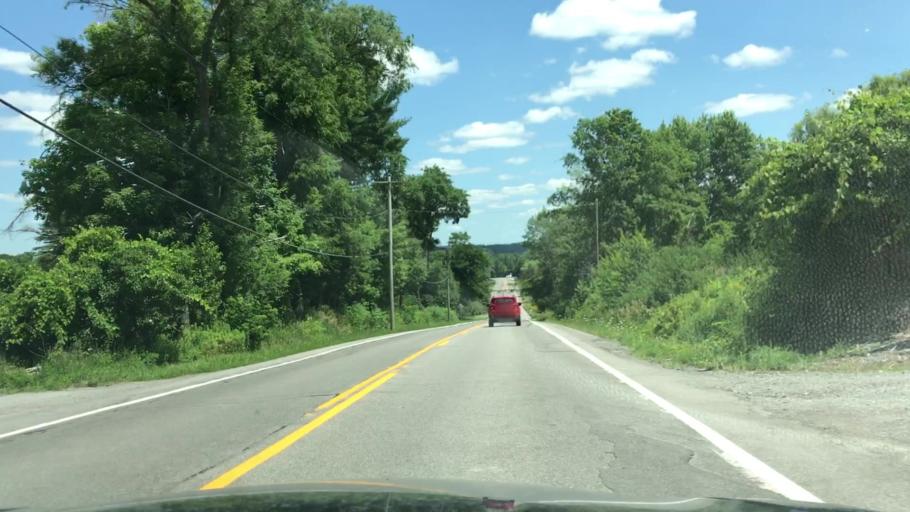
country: US
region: New York
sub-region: Erie County
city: East Aurora
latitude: 42.7677
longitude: -78.5589
